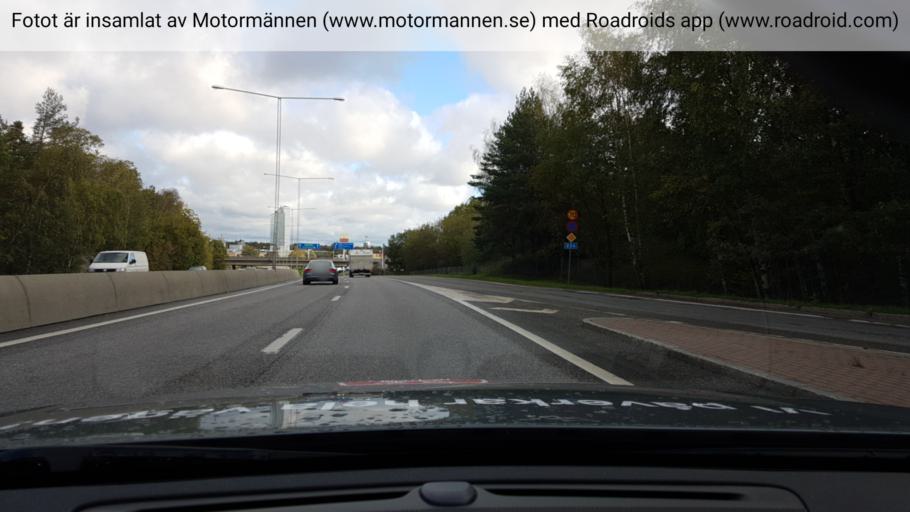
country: SE
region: Stockholm
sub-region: Huddinge Kommun
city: Huddinge
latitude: 59.2695
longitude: 18.0087
